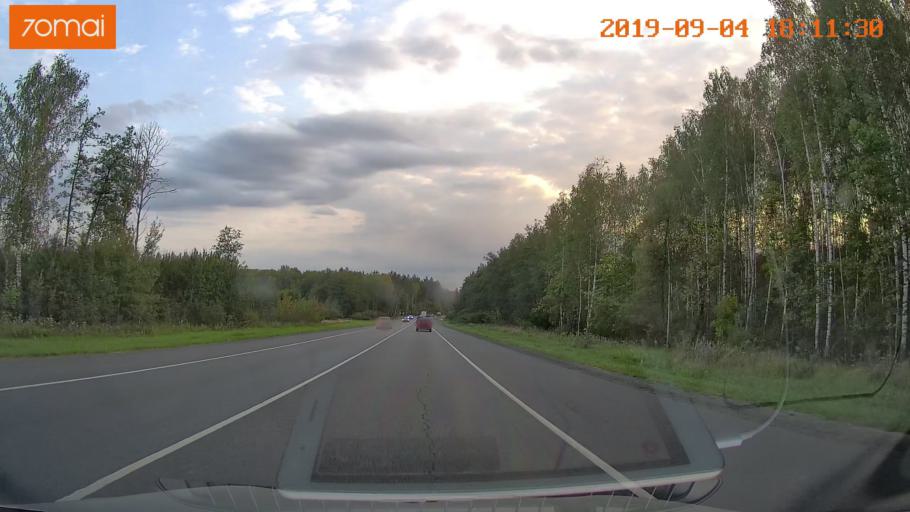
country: RU
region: Moskovskaya
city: Lopatinskiy
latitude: 55.3775
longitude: 38.7540
